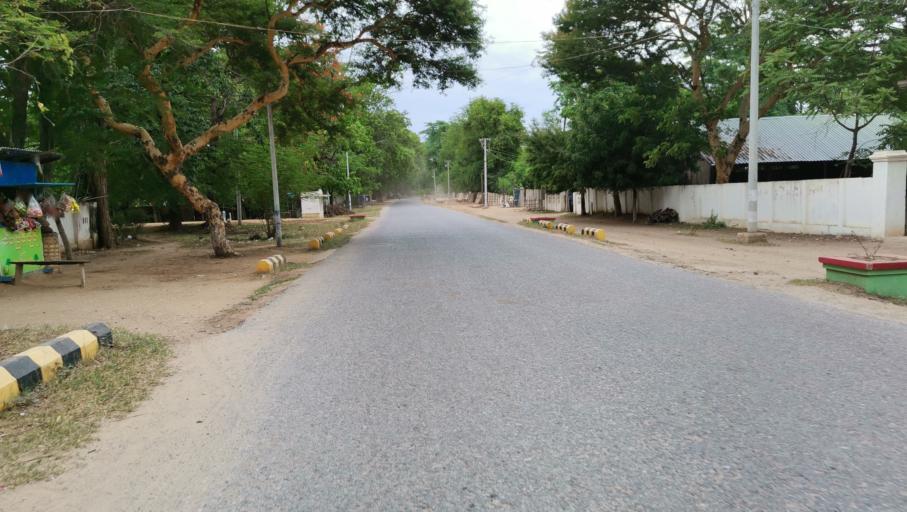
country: MM
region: Mandalay
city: Myingyan
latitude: 21.8415
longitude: 95.4269
